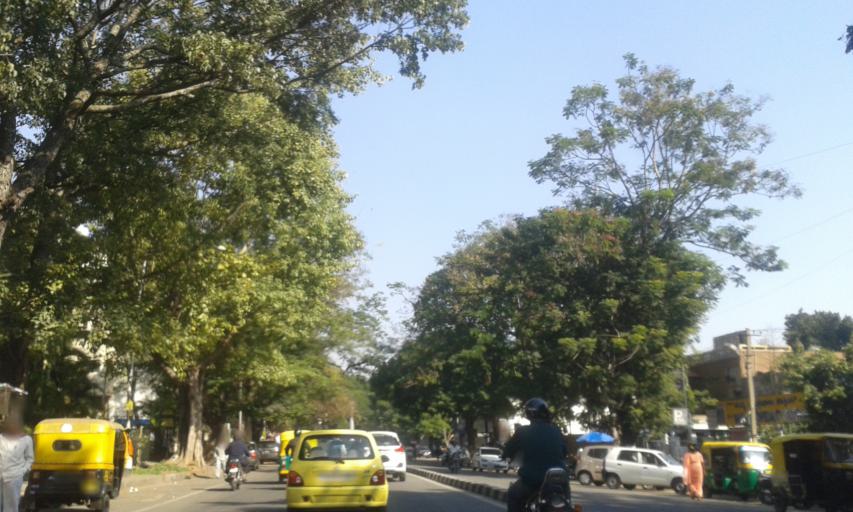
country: IN
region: Karnataka
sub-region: Bangalore Urban
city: Bangalore
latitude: 12.9423
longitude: 77.5852
